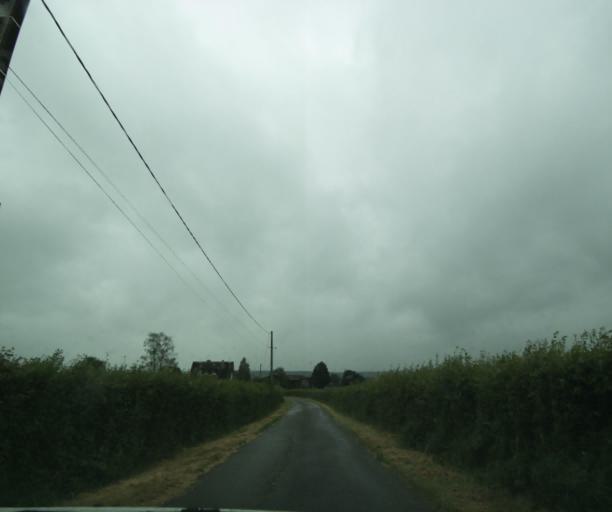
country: FR
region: Bourgogne
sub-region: Departement de Saone-et-Loire
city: Palinges
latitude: 46.5144
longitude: 4.2033
